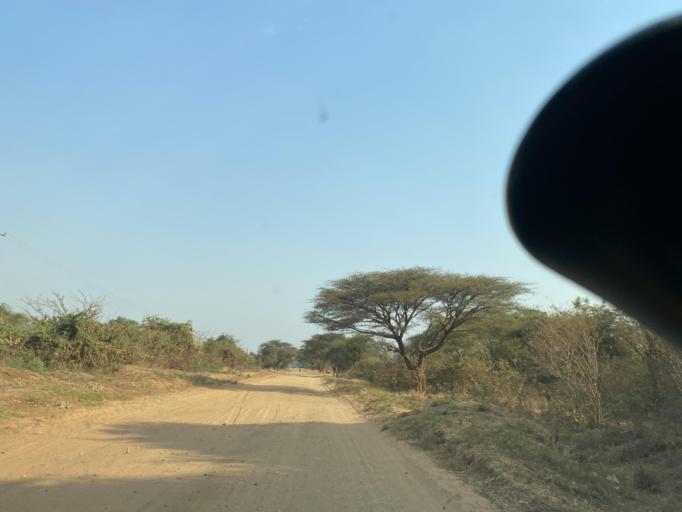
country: ZW
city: Chirundu
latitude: -15.9333
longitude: 28.8713
